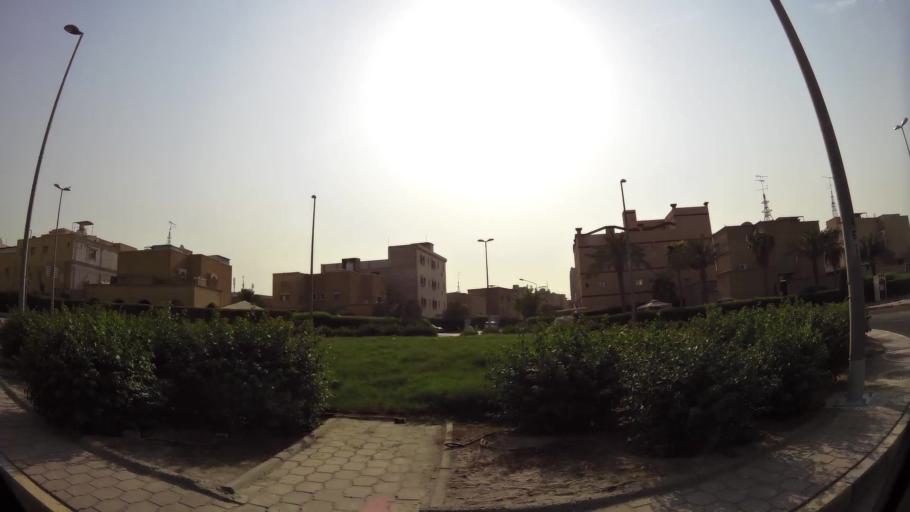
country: KW
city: Al Funaytis
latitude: 29.2221
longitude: 48.0797
